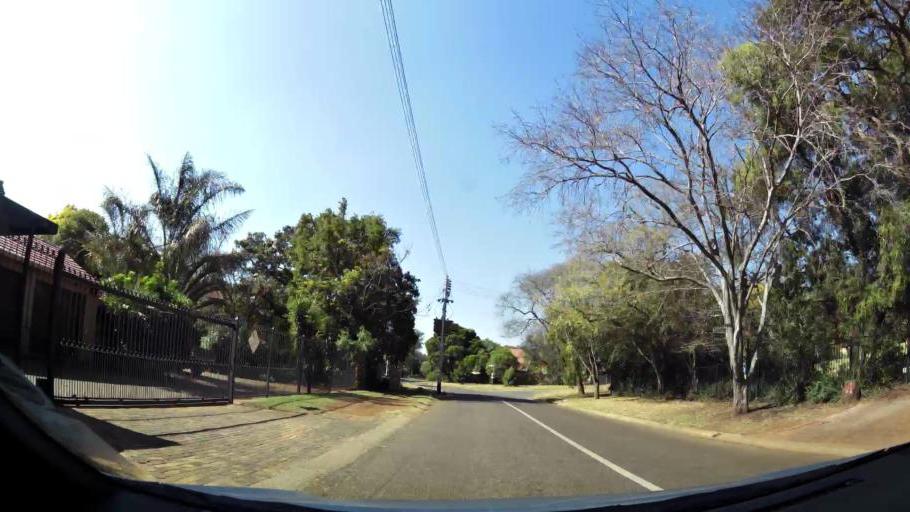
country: ZA
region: Gauteng
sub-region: City of Tshwane Metropolitan Municipality
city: Pretoria
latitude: -25.7682
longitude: 28.2703
